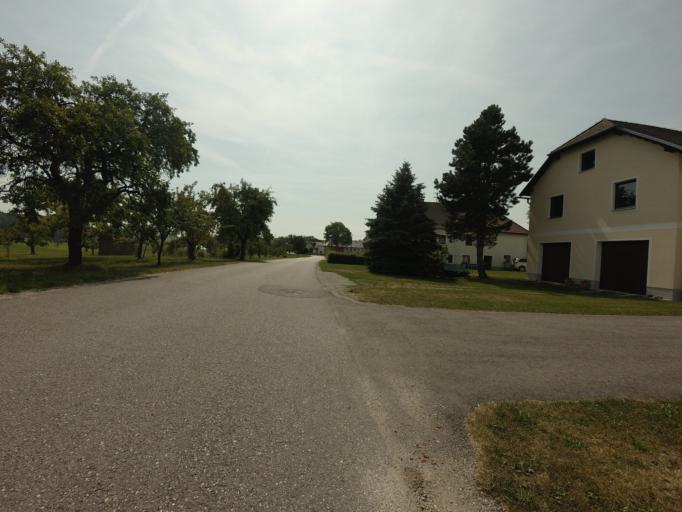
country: AT
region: Upper Austria
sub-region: Politischer Bezirk Urfahr-Umgebung
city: Reichenthal
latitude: 48.5322
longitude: 14.3631
